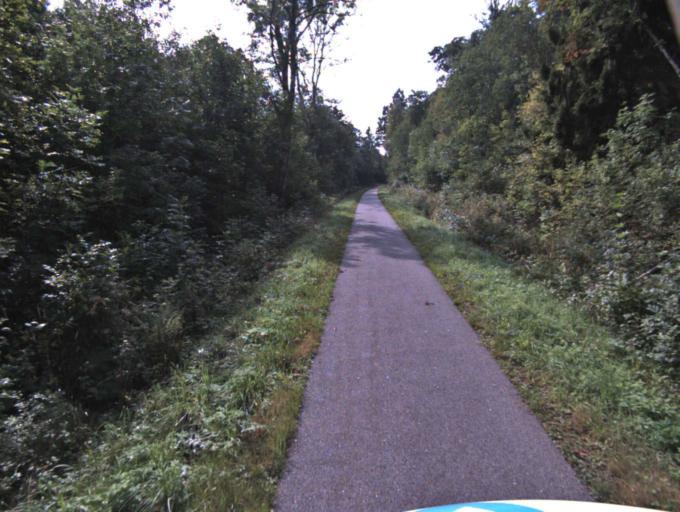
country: SE
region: Vaestra Goetaland
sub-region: Tranemo Kommun
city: Limmared
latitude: 57.6586
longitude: 13.3626
